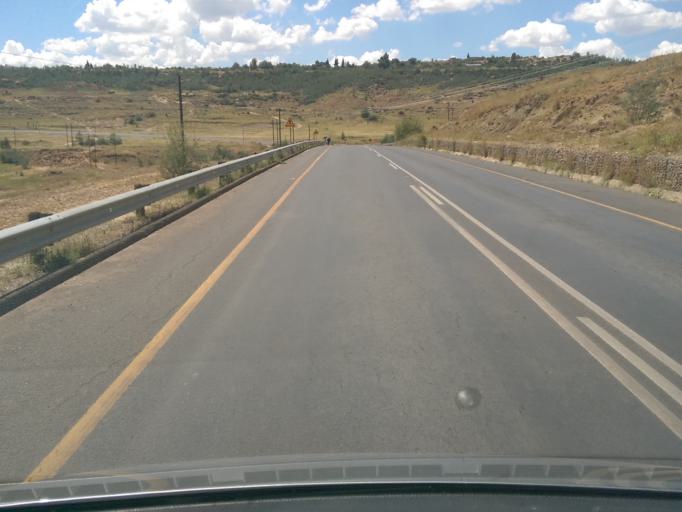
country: LS
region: Maseru
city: Maseru
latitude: -29.3844
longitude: 27.5033
